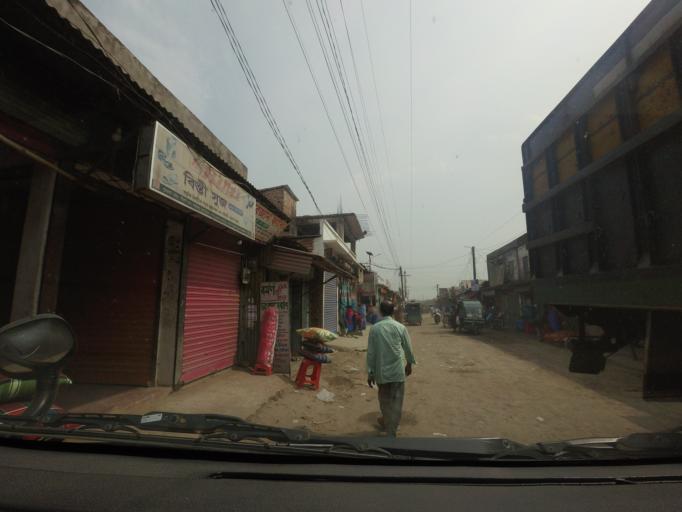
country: BD
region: Dhaka
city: Kishorganj
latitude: 24.3470
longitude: 90.7558
